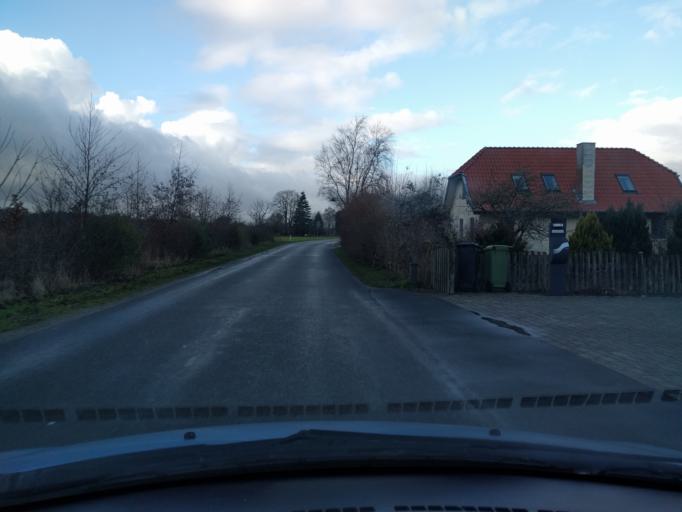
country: DK
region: South Denmark
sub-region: Kerteminde Kommune
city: Langeskov
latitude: 55.3939
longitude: 10.5602
